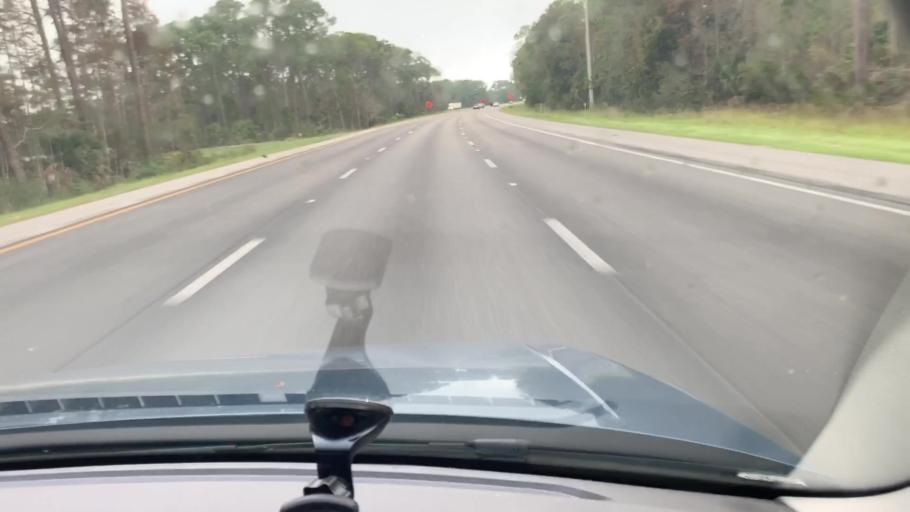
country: US
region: Florida
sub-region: Volusia County
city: Port Orange
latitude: 29.1303
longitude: -81.0598
